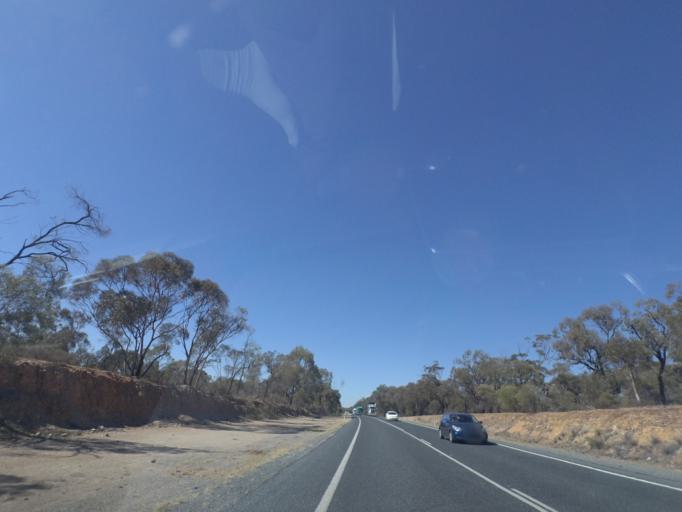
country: AU
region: New South Wales
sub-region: Bland
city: West Wyalong
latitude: -34.1389
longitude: 147.1206
